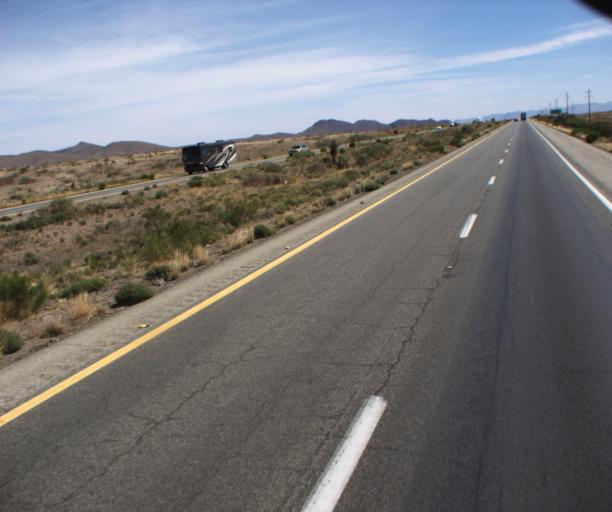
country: US
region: Arizona
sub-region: Cochise County
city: Willcox
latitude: 32.3609
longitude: -109.6616
